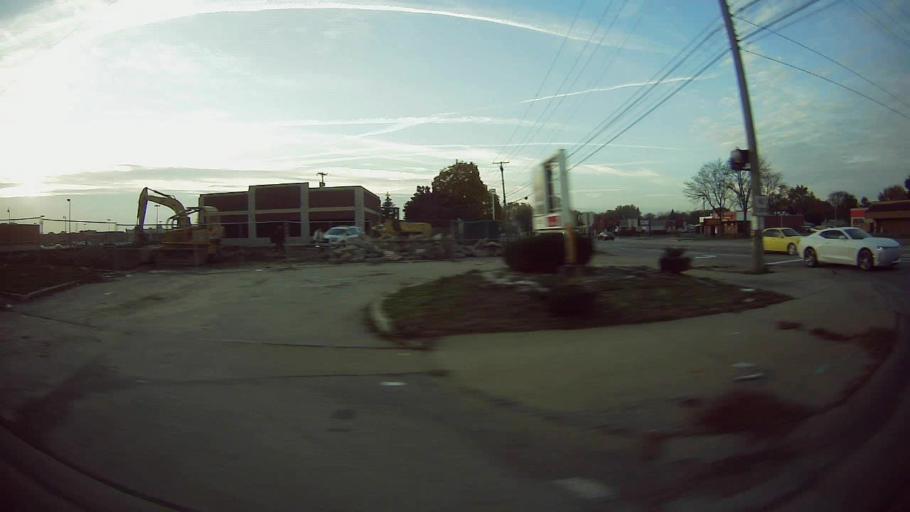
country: US
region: Michigan
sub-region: Macomb County
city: Sterling Heights
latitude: 42.5638
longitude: -83.0885
